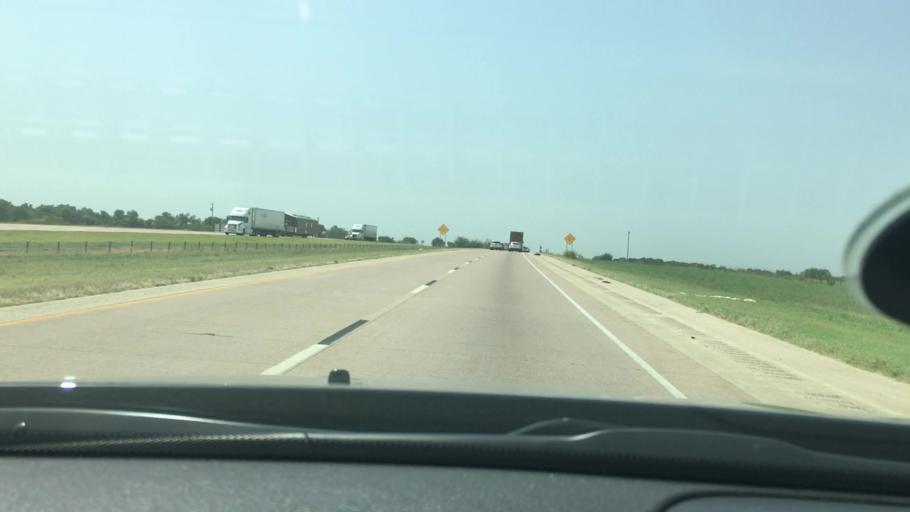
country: US
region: Oklahoma
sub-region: Garvin County
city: Pauls Valley
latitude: 34.6842
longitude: -97.2295
